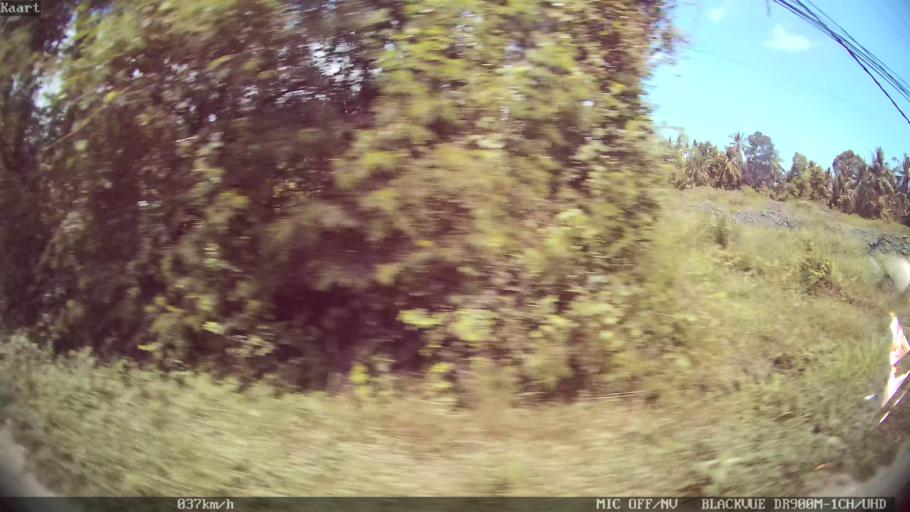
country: ID
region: Bali
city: Banjar Padangbulia
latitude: -8.1576
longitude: 115.1135
